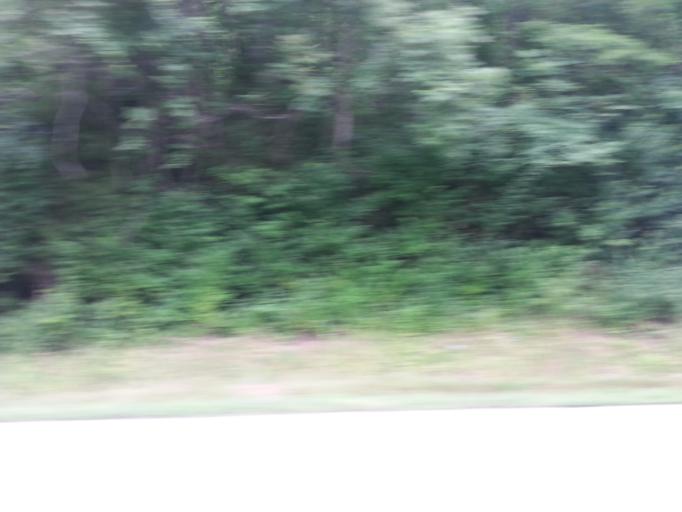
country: US
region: Ohio
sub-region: Brown County
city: Aberdeen
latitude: 38.7036
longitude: -83.7923
